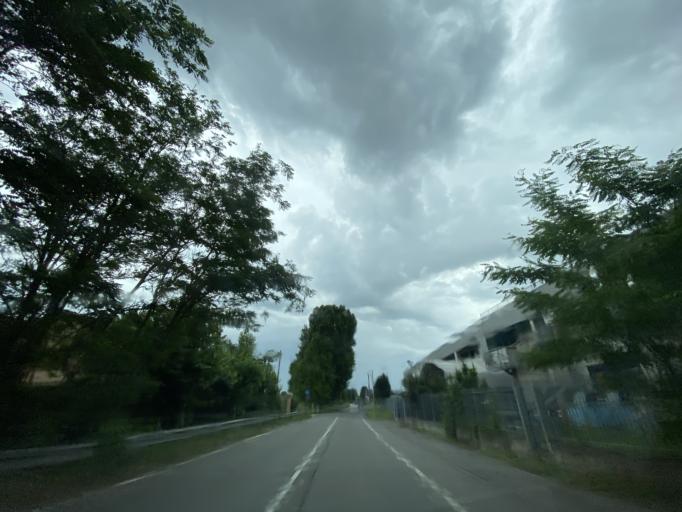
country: IT
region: Lombardy
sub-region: Provincia di Monza e Brianza
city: Brugherio
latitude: 45.5602
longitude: 9.2865
